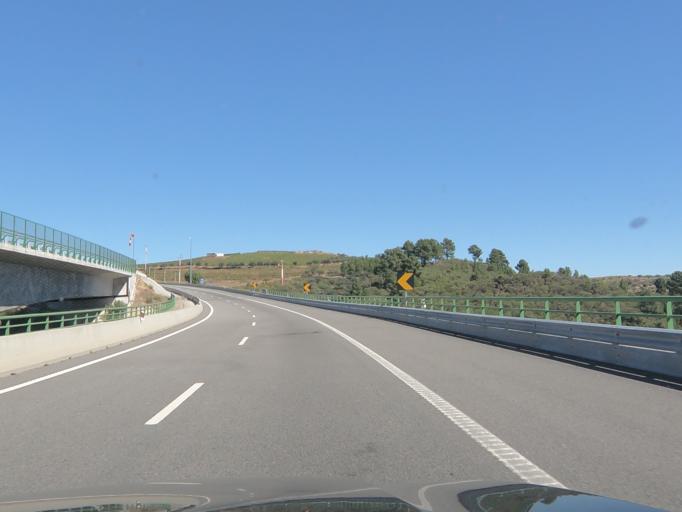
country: PT
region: Vila Real
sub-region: Murca
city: Murca
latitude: 41.3914
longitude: -7.4503
